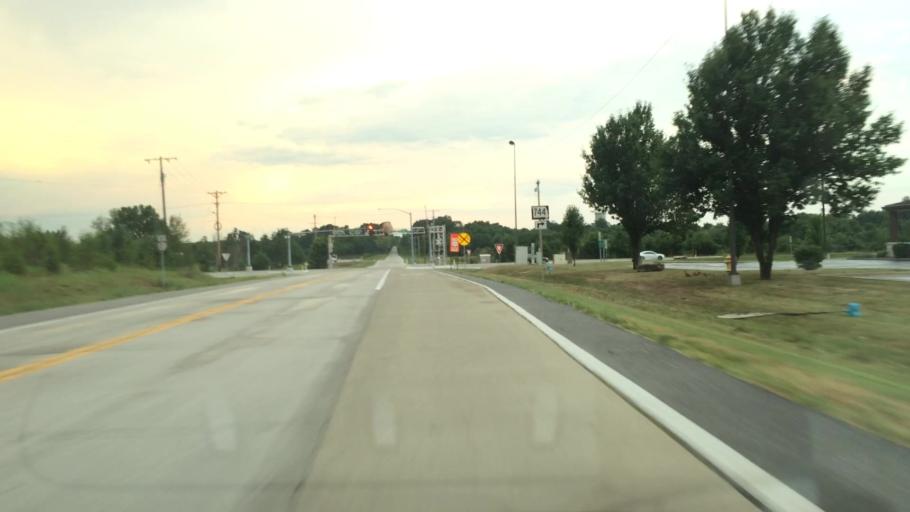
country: US
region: Missouri
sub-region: Greene County
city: Strafford
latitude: 37.2486
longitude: -93.1834
